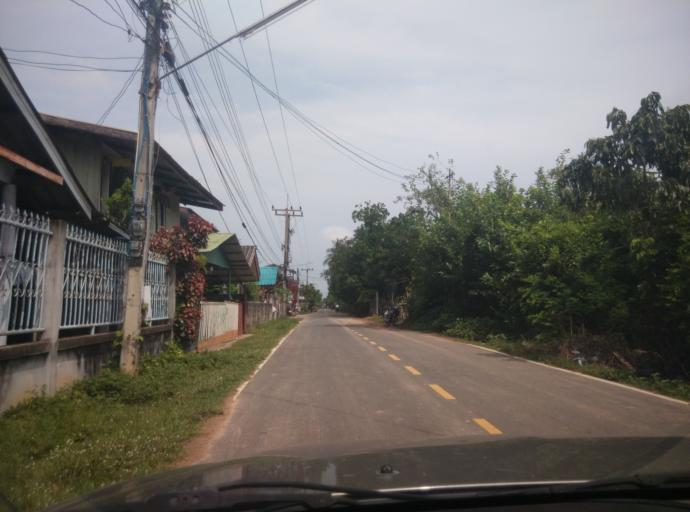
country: TH
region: Sisaket
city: Huai Thap Than
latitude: 15.0282
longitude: 104.0730
